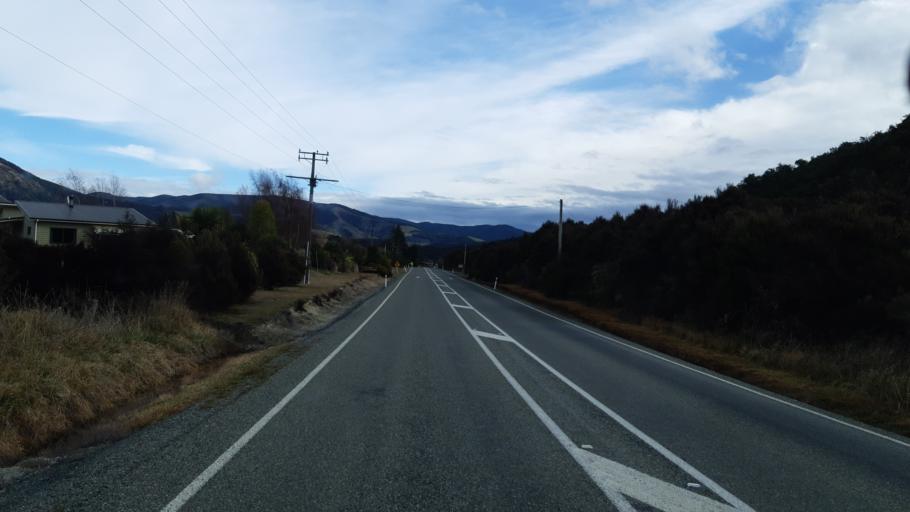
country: NZ
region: Tasman
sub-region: Tasman District
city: Wakefield
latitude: -41.8009
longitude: 172.8577
